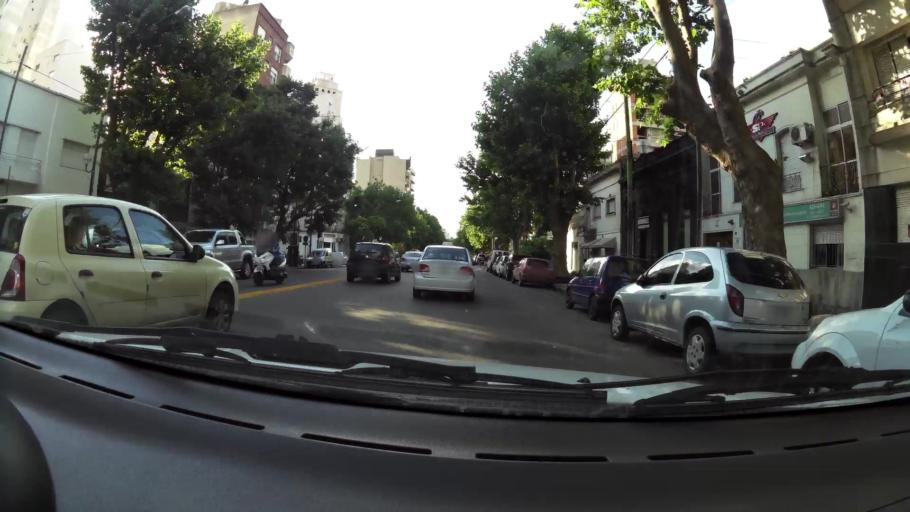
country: AR
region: Buenos Aires
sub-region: Partido de La Plata
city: La Plata
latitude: -34.9185
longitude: -57.9586
